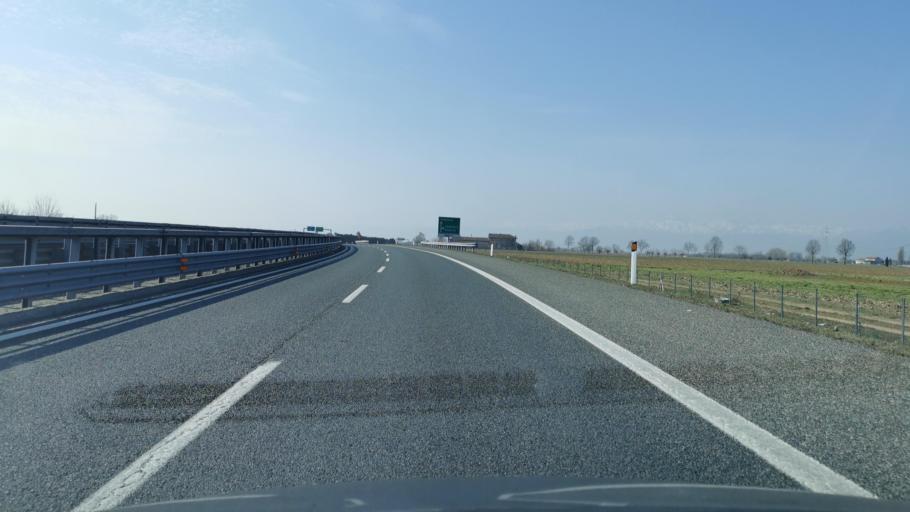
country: IT
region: Piedmont
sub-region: Provincia di Torino
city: Pasta
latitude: 44.9928
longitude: 7.5613
